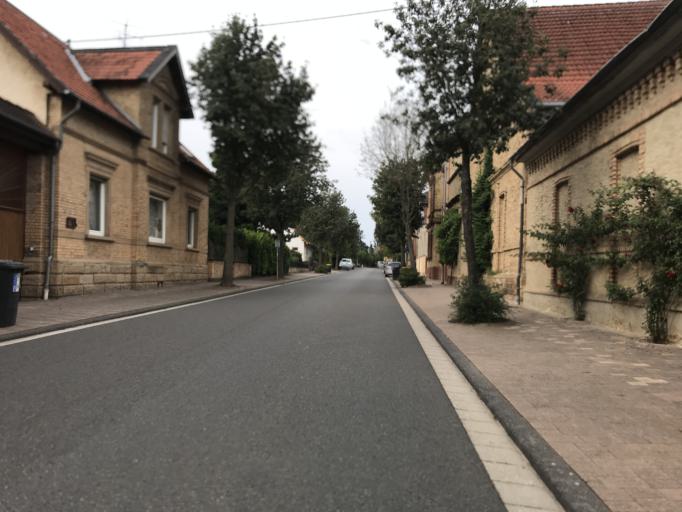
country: DE
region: Rheinland-Pfalz
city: Sankt Johann
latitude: 49.8681
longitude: 8.0170
